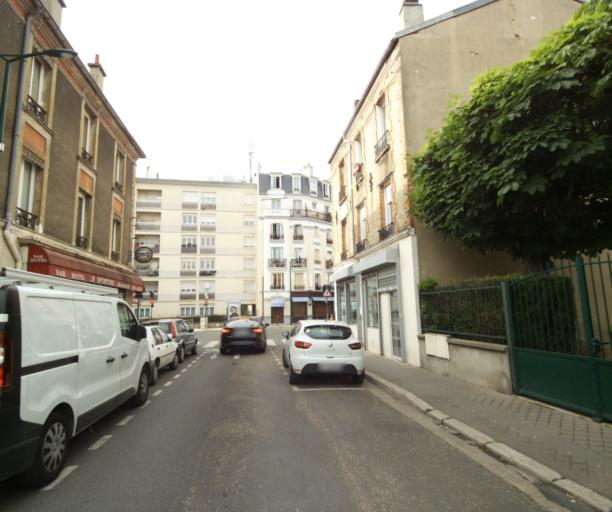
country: FR
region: Ile-de-France
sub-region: Departement des Hauts-de-Seine
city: La Garenne-Colombes
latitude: 48.9130
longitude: 2.2407
